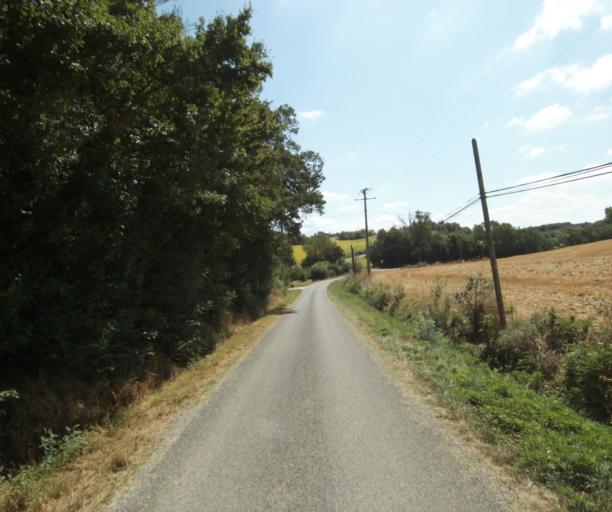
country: FR
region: Midi-Pyrenees
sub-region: Departement de la Haute-Garonne
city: Auriac-sur-Vendinelle
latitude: 43.4823
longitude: 1.8440
